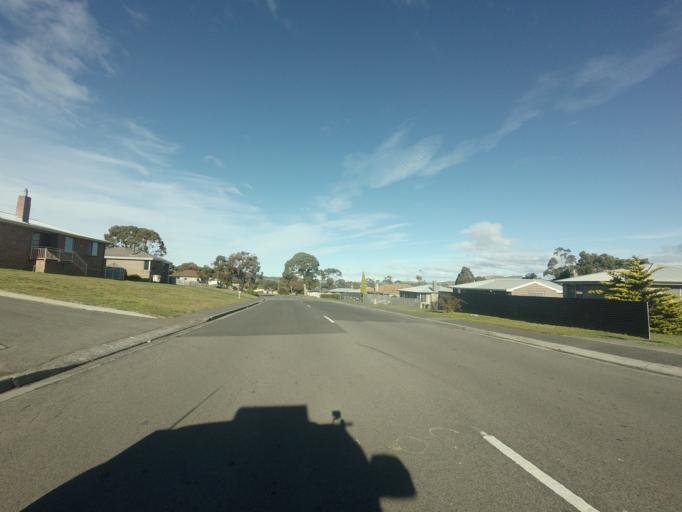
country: AU
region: Tasmania
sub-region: Clarence
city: Rokeby
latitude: -42.8923
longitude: 147.4424
